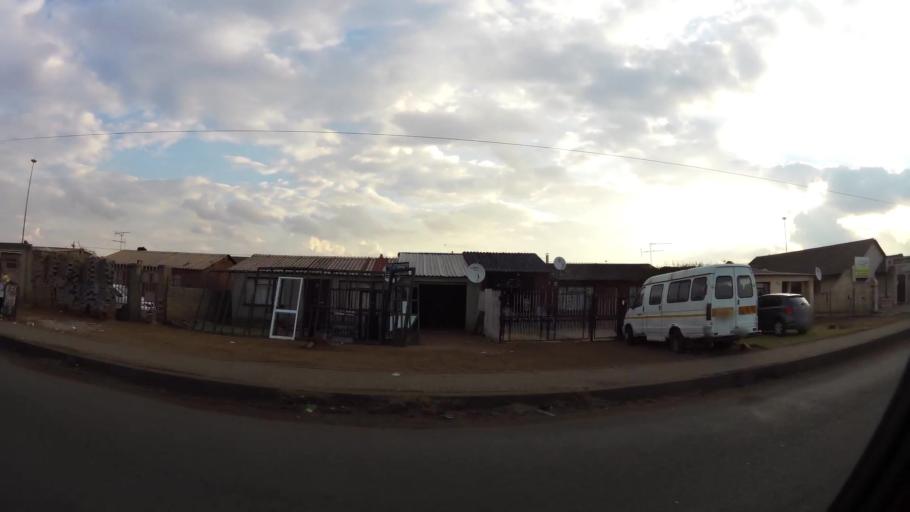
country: ZA
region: Gauteng
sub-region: City of Johannesburg Metropolitan Municipality
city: Orange Farm
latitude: -26.5817
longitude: 27.8430
